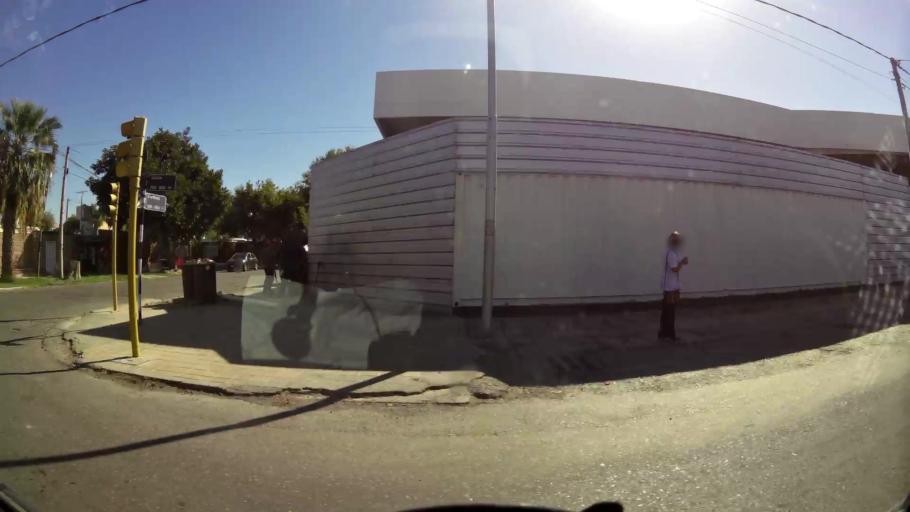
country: AR
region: San Juan
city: San Juan
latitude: -31.5260
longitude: -68.5362
